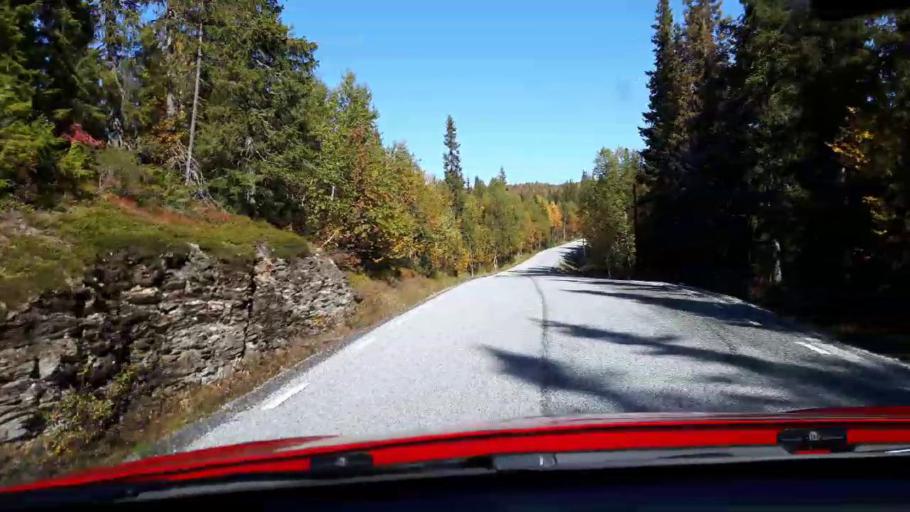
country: NO
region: Nord-Trondelag
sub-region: Royrvik
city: Royrvik
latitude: 64.8132
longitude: 14.1750
